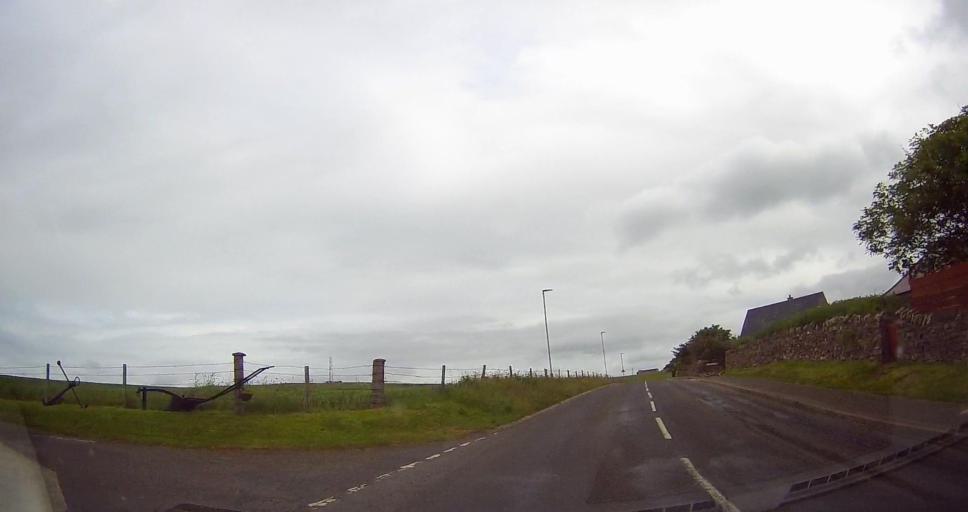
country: GB
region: Scotland
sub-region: Orkney Islands
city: Stromness
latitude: 58.9707
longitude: -3.2878
